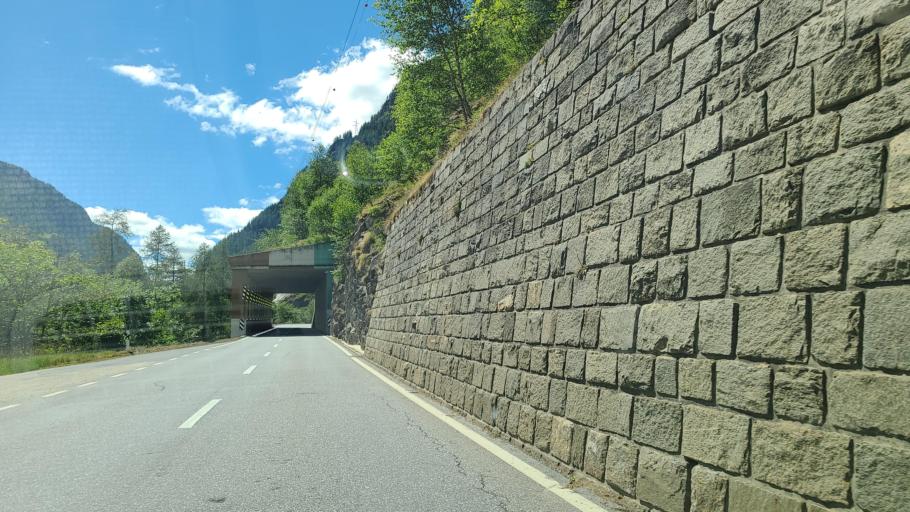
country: CH
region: Valais
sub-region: Visp District
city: Stalden
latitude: 46.2084
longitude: 7.8876
